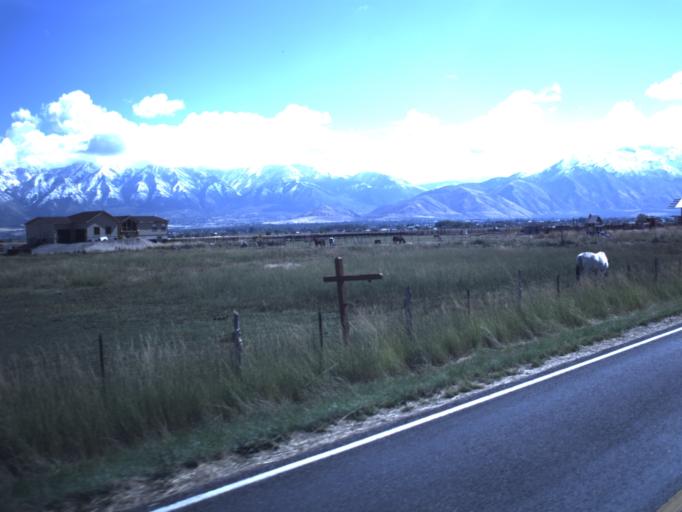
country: US
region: Utah
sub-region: Utah County
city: West Mountain
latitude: 40.0946
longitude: -111.7881
